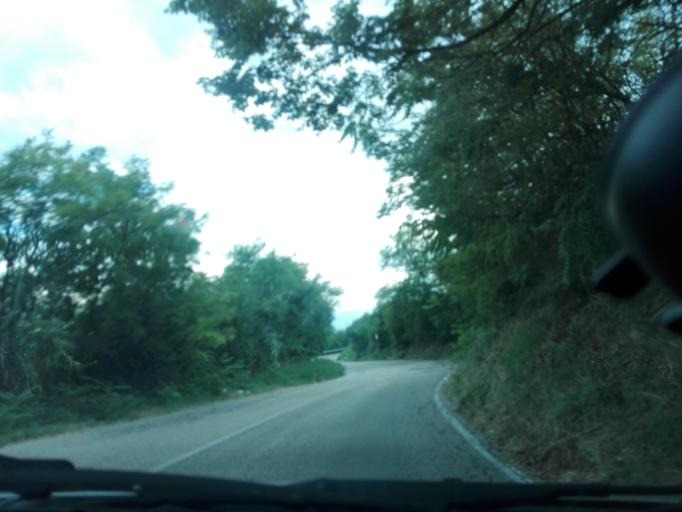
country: IT
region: Abruzzo
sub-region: Provincia di Pescara
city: Spoltore
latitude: 42.4748
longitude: 14.1360
